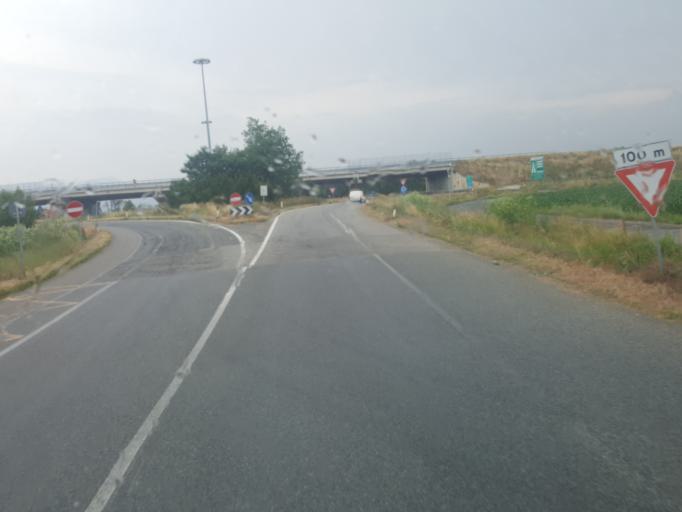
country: IT
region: Piedmont
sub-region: Provincia di Torino
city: Orbassano
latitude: 44.9796
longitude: 7.5542
